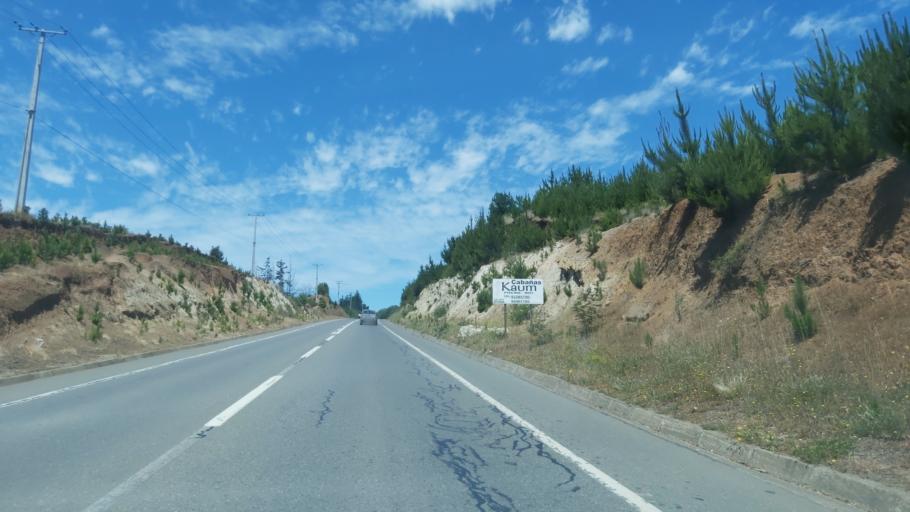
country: CL
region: Maule
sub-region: Provincia de Talca
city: Constitucion
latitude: -35.3211
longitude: -72.3854
